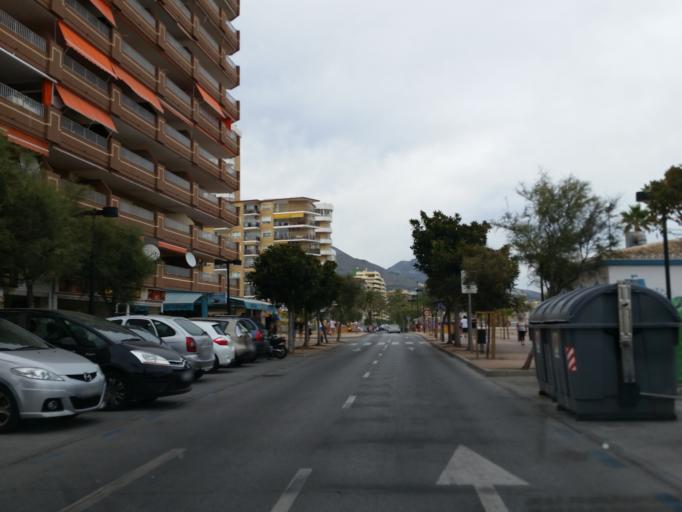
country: ES
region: Andalusia
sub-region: Provincia de Malaga
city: Fuengirola
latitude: 36.5549
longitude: -4.6119
